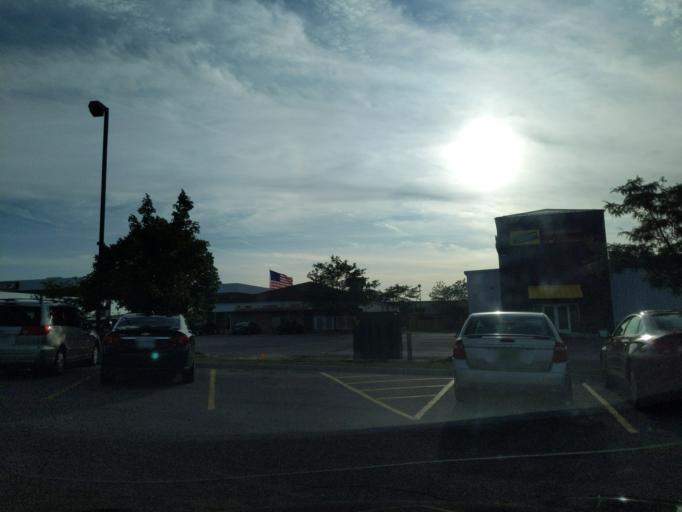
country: US
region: Michigan
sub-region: Eaton County
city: Waverly
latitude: 42.7419
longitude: -84.6777
